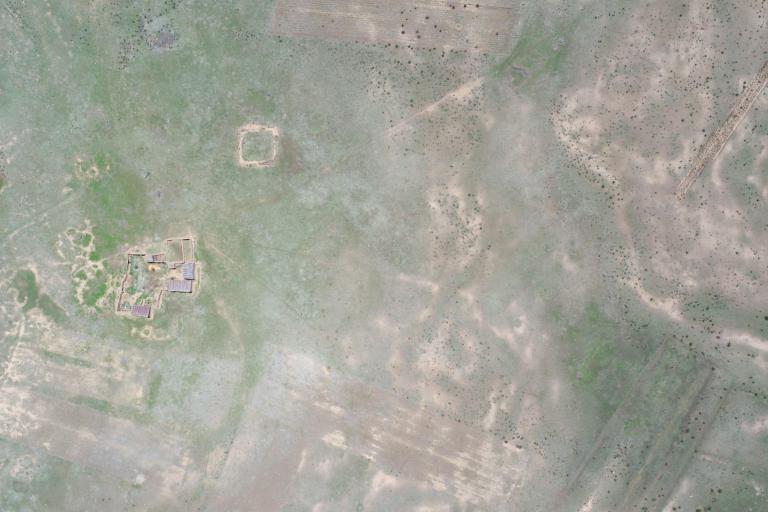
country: BO
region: La Paz
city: Curahuara de Carangas
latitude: -17.2764
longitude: -68.5176
